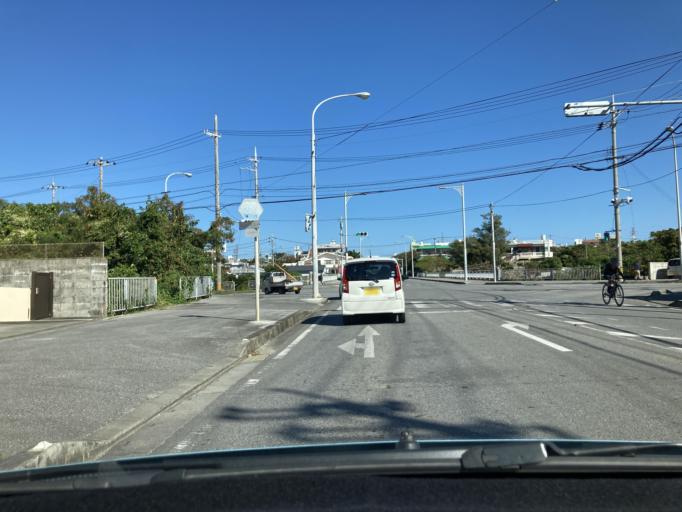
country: JP
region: Okinawa
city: Gushikawa
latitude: 26.3784
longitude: 127.8652
